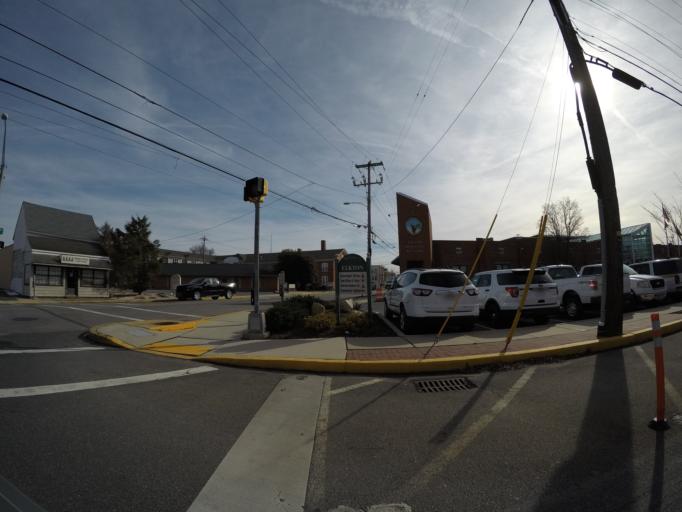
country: US
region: Maryland
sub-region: Cecil County
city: Elkton
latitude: 39.6110
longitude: -75.8306
